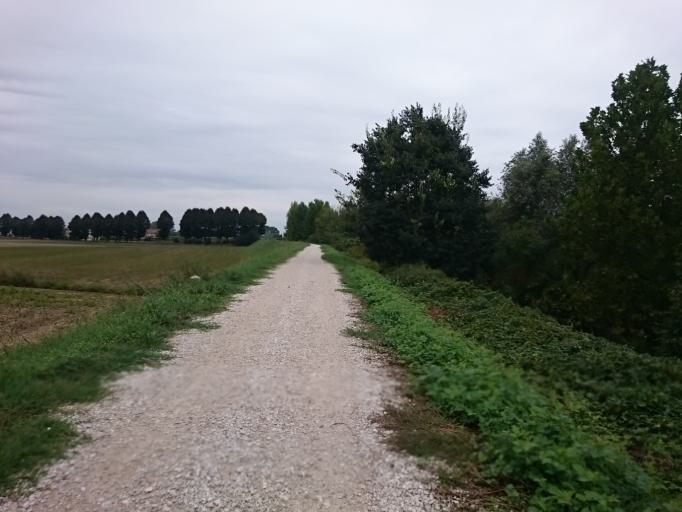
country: IT
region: Veneto
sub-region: Provincia di Vicenza
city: Quinto Vicentino
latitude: 45.5698
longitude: 11.6266
